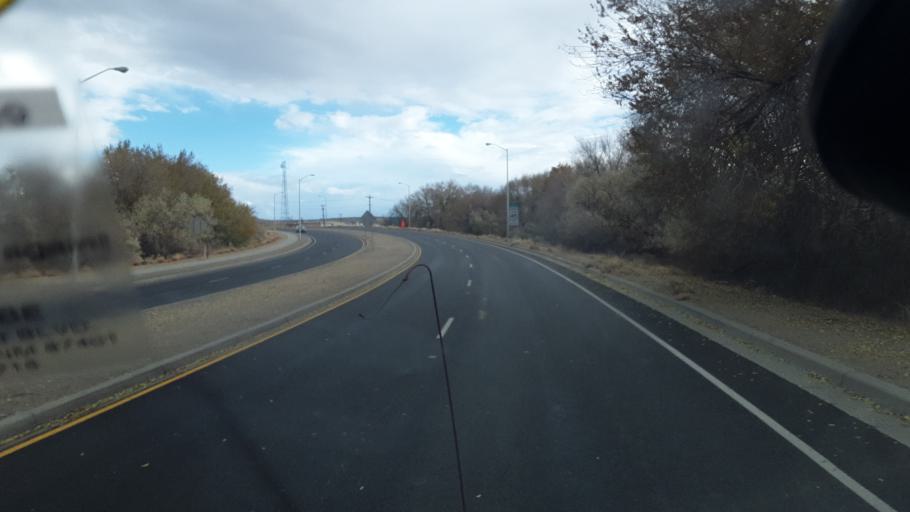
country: US
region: New Mexico
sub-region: San Juan County
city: Farmington
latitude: 36.7207
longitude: -108.2210
